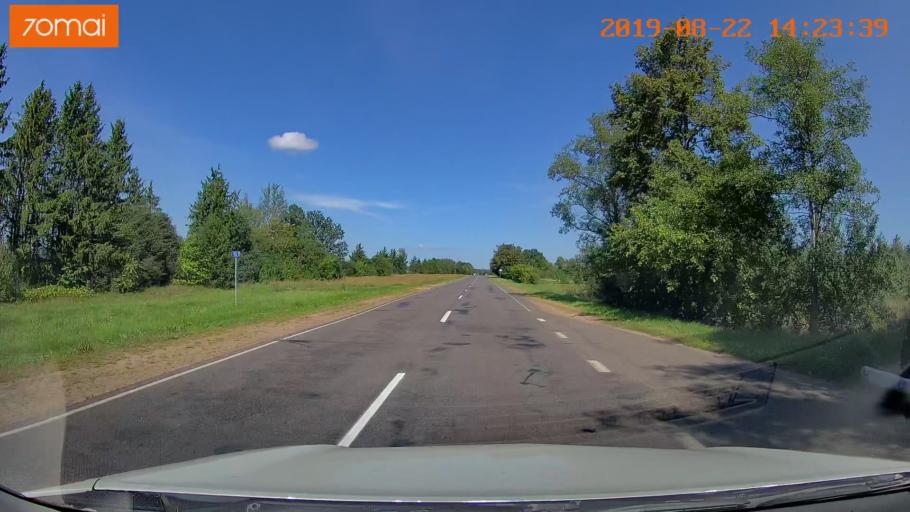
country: BY
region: Mogilev
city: Asipovichy
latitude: 53.2913
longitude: 28.5869
